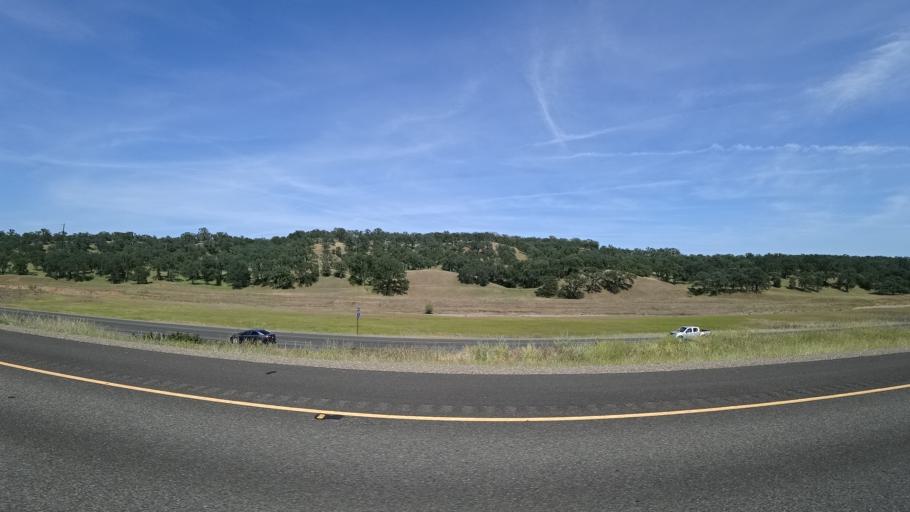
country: US
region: California
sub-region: Tehama County
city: Red Bluff
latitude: 40.2416
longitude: -122.2585
